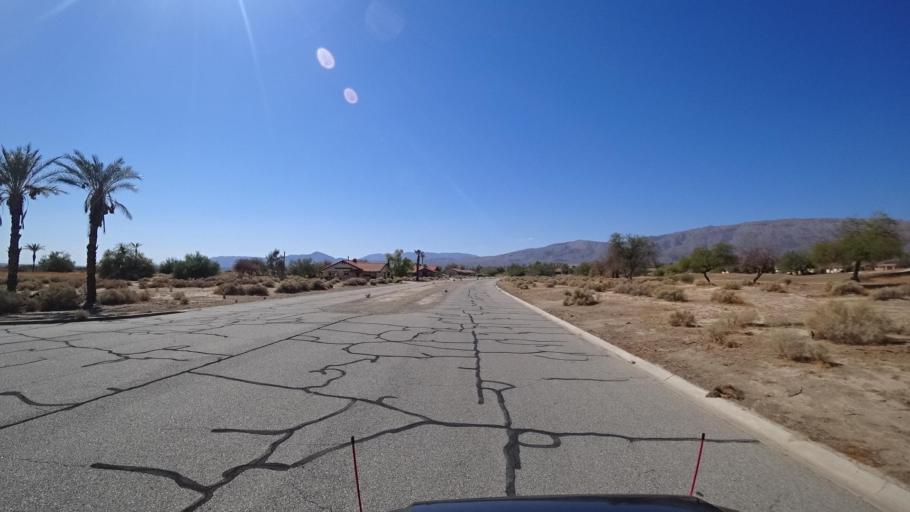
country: US
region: California
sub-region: San Diego County
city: Borrego Springs
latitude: 33.2439
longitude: -116.3515
